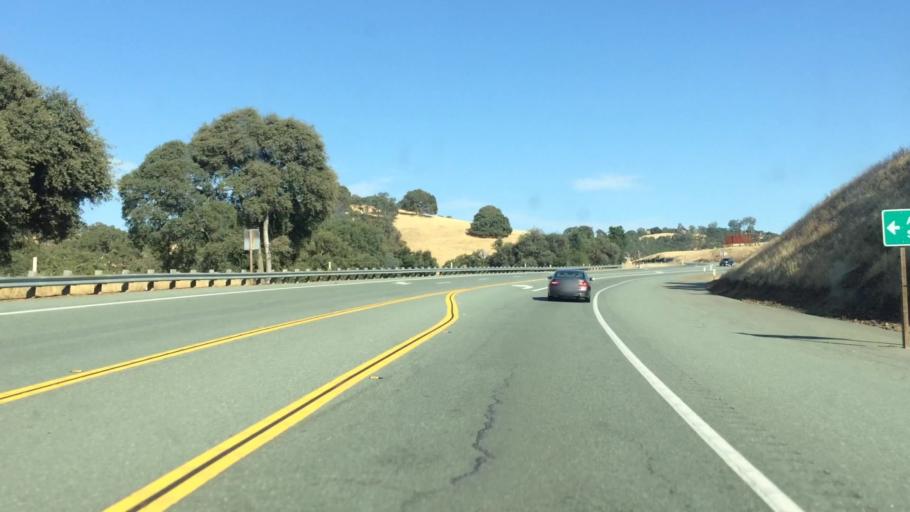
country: US
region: California
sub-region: Amador County
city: Sutter Creek
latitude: 38.4217
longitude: -120.8429
